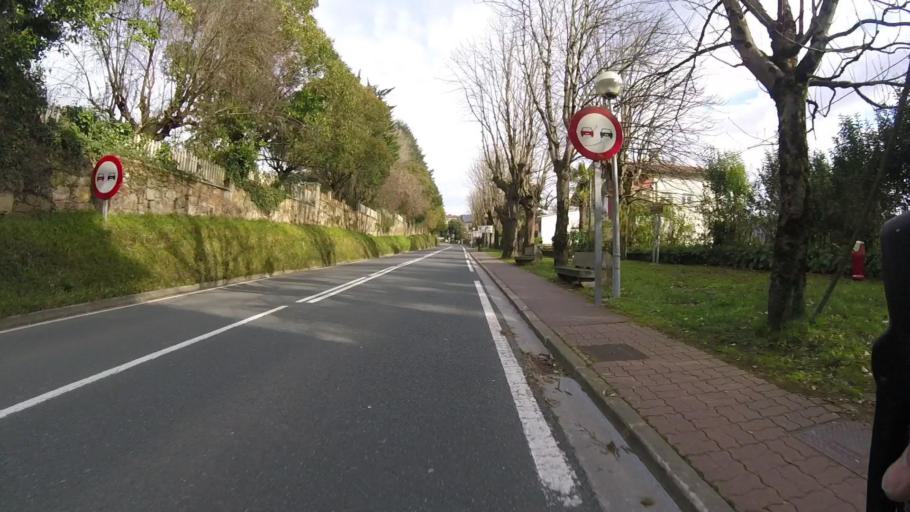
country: ES
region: Basque Country
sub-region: Provincia de Guipuzcoa
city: Lezo
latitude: 43.3004
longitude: -1.8649
